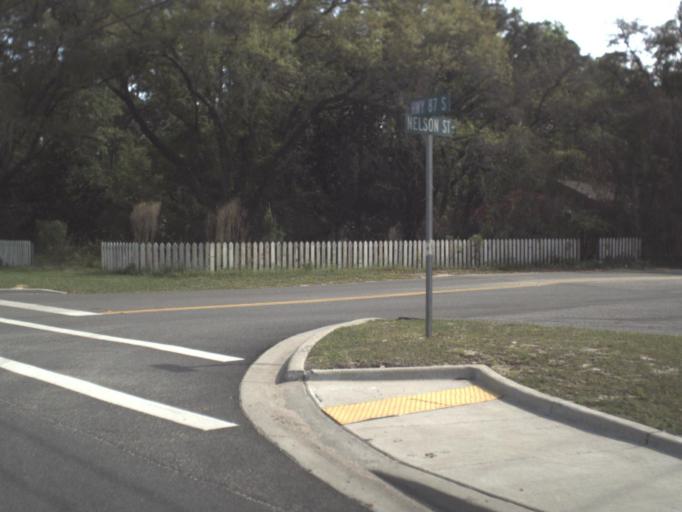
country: US
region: Florida
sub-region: Santa Rosa County
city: Holley
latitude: 30.4527
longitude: -86.9078
